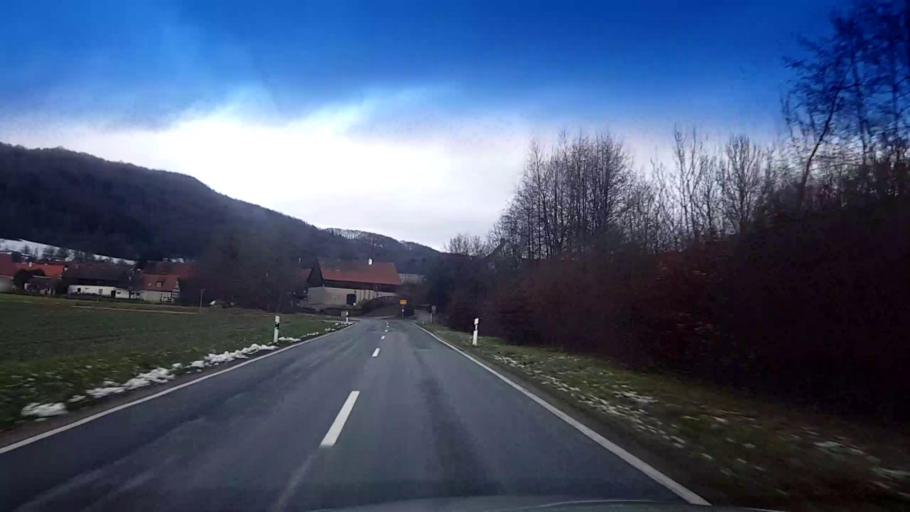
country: DE
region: Bavaria
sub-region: Upper Franconia
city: Buttenheim
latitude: 49.8293
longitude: 11.0786
